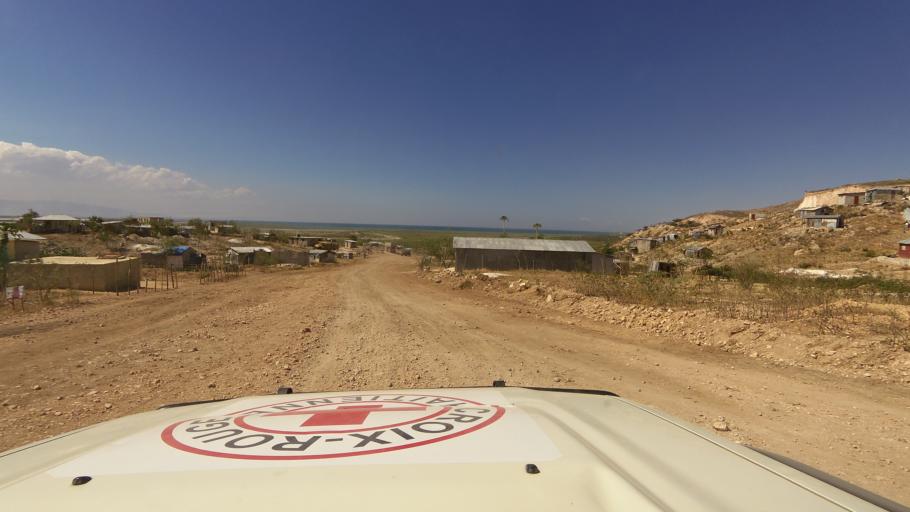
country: HT
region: Ouest
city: Croix des Bouquets
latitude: 18.6669
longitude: -72.2955
